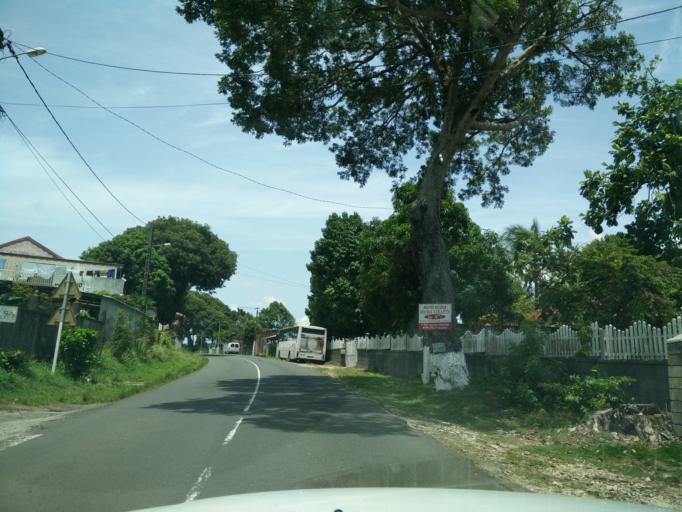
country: GP
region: Guadeloupe
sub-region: Guadeloupe
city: Petit-Bourg
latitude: 16.1839
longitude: -61.5884
